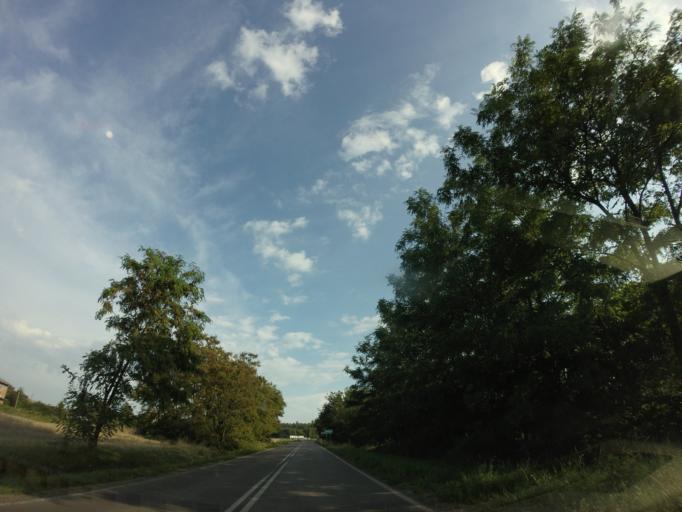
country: PL
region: Lublin Voivodeship
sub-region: Powiat lubartowski
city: Michow
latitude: 51.5644
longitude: 22.2966
